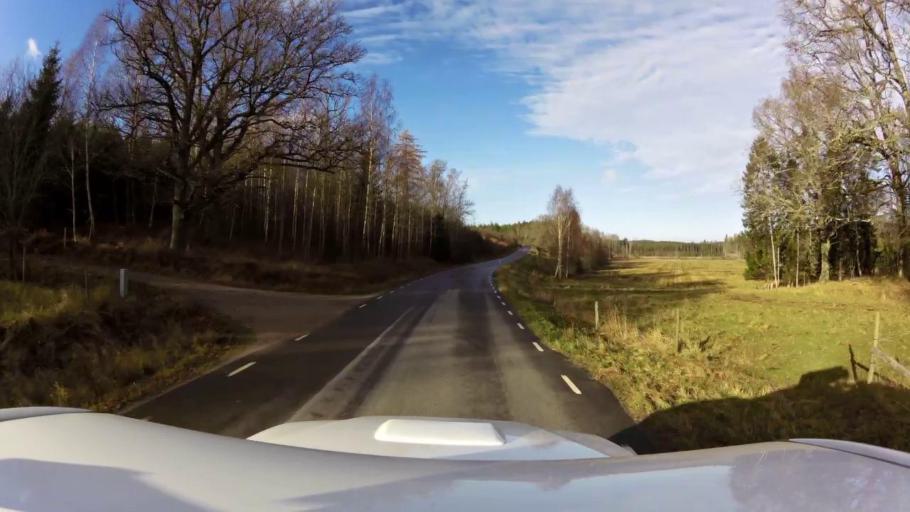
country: SE
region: OEstergoetland
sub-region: Linkopings Kommun
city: Sturefors
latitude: 58.3170
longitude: 15.6658
